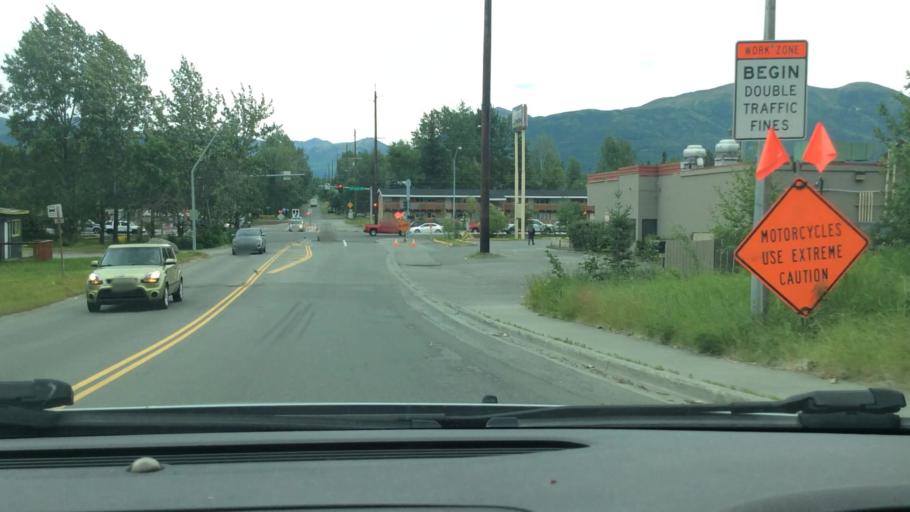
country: US
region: Alaska
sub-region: Anchorage Municipality
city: Elmendorf Air Force Base
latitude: 61.2242
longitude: -149.7357
